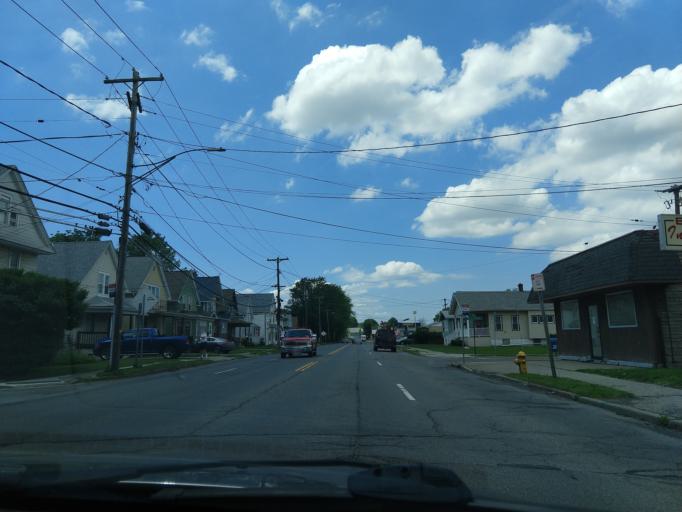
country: US
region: New York
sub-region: Erie County
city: West Seneca
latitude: 42.8460
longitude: -78.7983
